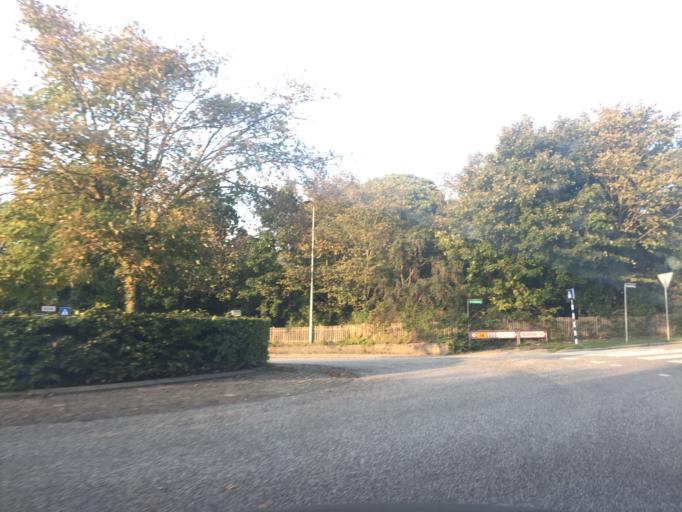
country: DK
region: Zealand
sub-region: Lejre Kommune
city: Kirke Hvalso
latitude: 55.5897
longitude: 11.8626
